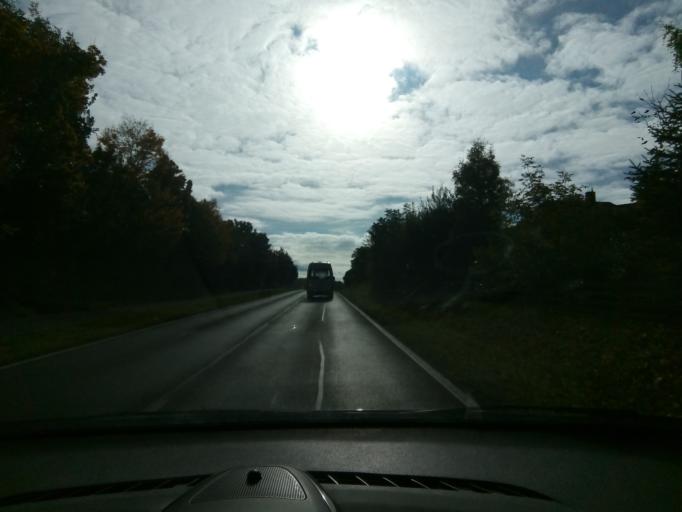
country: DE
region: Bavaria
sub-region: Regierungsbezirk Unterfranken
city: Gerolzhofen
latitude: 49.8946
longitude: 10.3539
